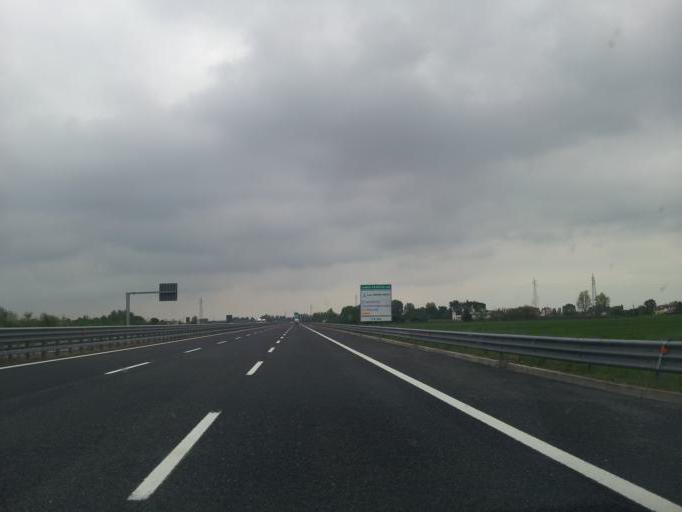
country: IT
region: Veneto
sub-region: Provincia di Treviso
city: Casale sul Sile
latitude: 45.5767
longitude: 12.3196
